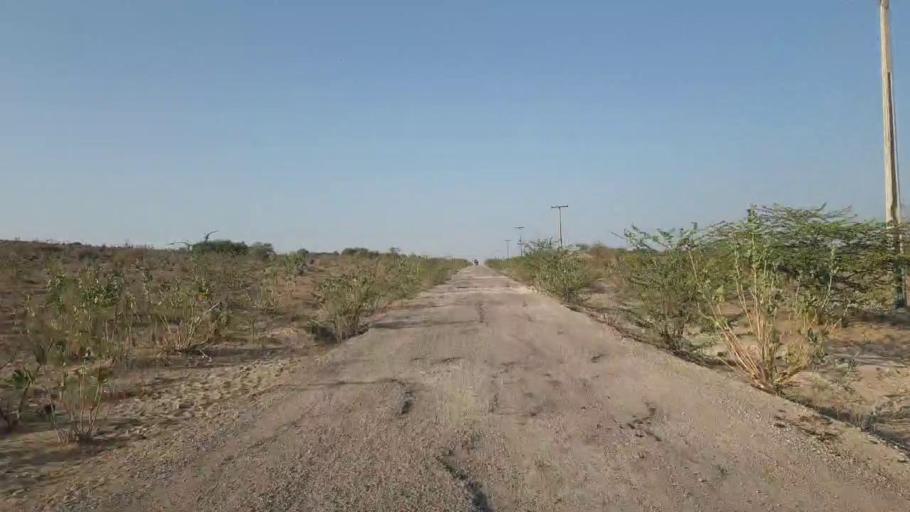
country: PK
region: Sindh
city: Chor
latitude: 25.6077
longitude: 69.8377
